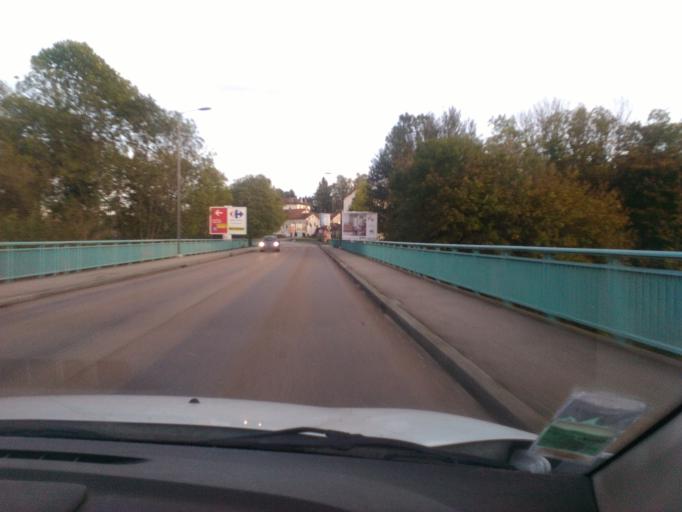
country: FR
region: Lorraine
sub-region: Departement des Vosges
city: Epinal
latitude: 48.1936
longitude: 6.4495
